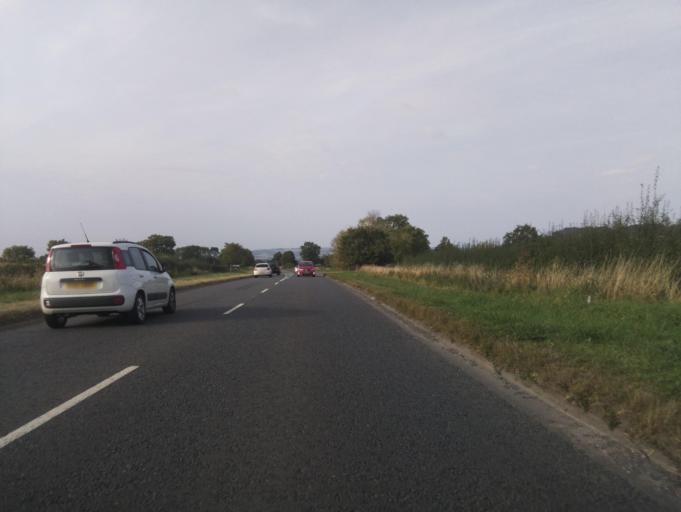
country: GB
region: England
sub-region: Gloucestershire
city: Gotherington
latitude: 51.9713
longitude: -2.0705
